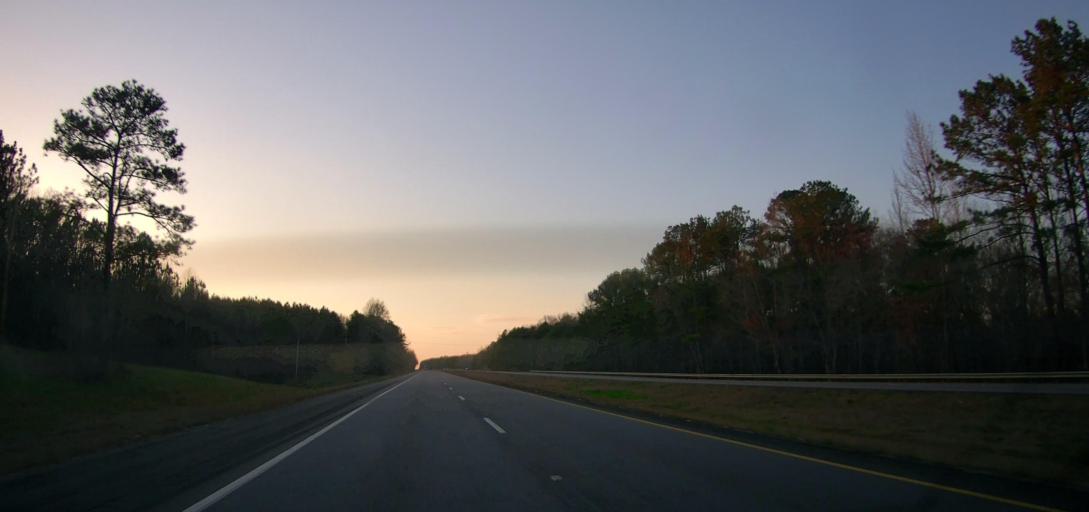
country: US
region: Alabama
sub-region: Coosa County
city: Goodwater
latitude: 33.0085
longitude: -86.0908
